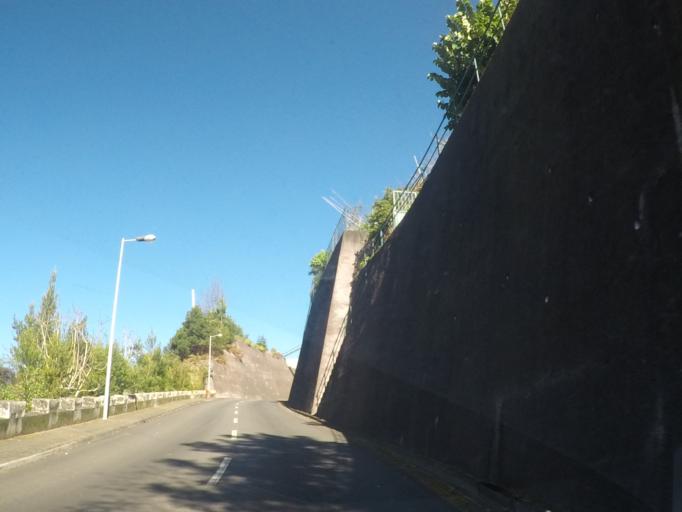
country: PT
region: Madeira
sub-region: Santana
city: Santana
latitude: 32.8023
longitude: -16.9621
